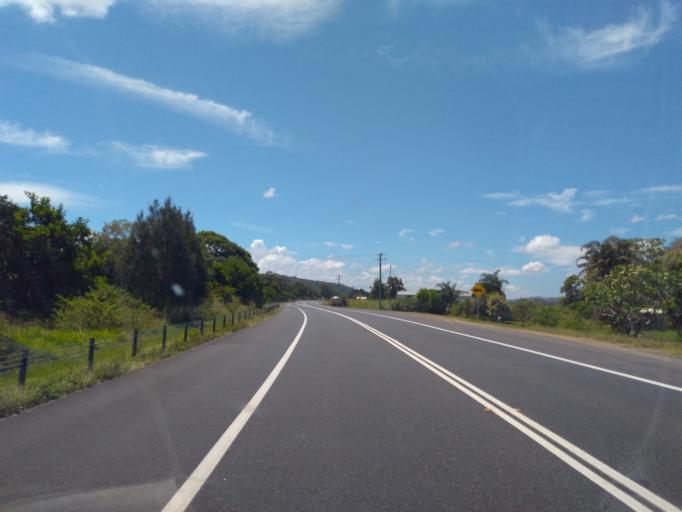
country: AU
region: New South Wales
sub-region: Clarence Valley
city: Maclean
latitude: -29.5305
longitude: 153.1868
